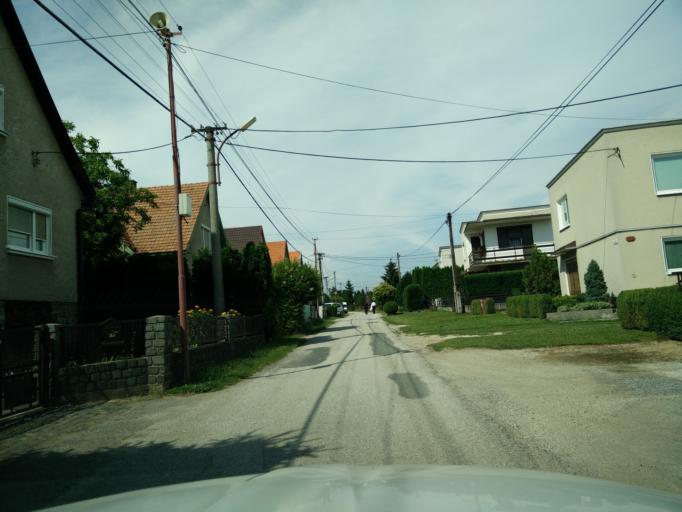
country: SK
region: Nitriansky
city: Prievidza
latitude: 48.8163
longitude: 18.6166
